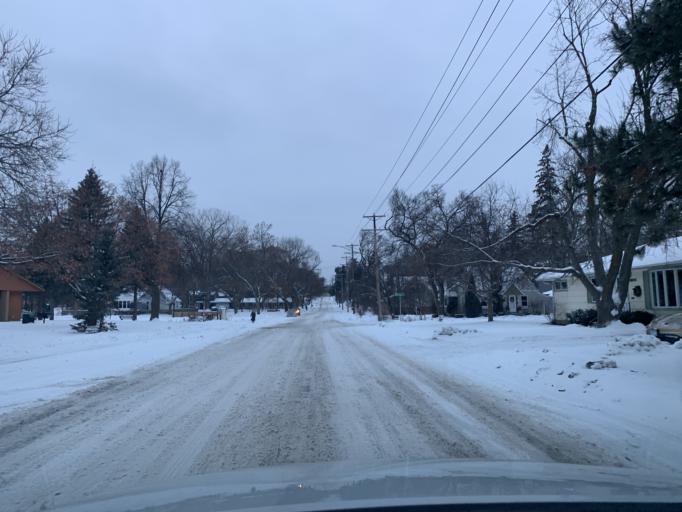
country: US
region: Minnesota
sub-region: Hennepin County
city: Saint Louis Park
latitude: 44.9234
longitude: -93.3425
